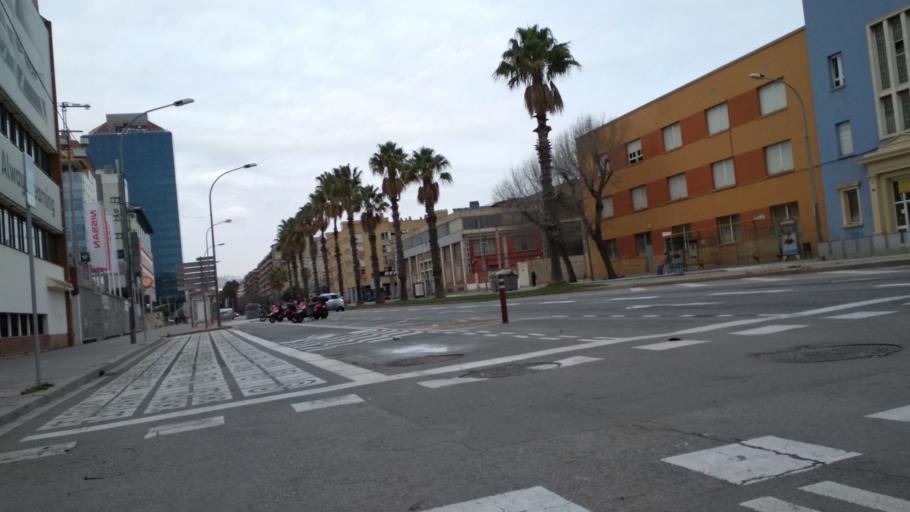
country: ES
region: Catalonia
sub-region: Provincia de Barcelona
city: Sants-Montjuic
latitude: 41.3543
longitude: 2.1432
